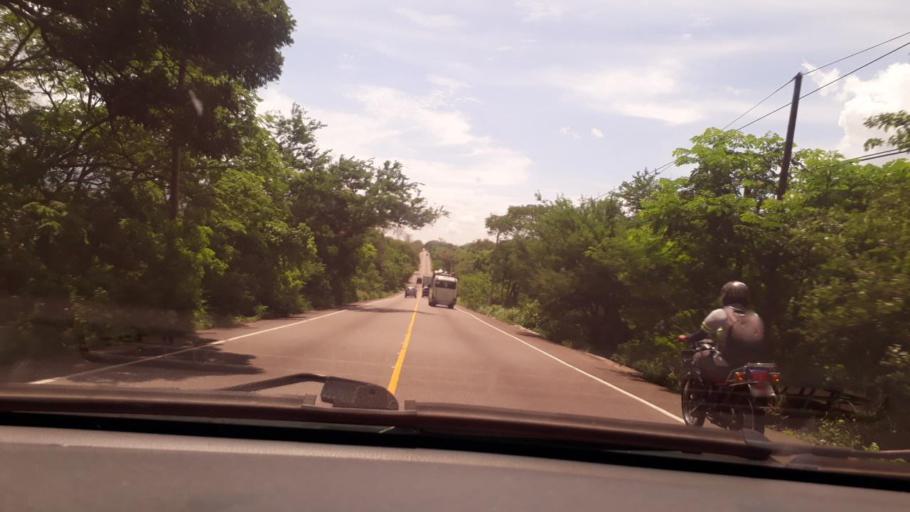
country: GT
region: Zacapa
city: Rio Hondo
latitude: 15.0550
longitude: -89.5558
